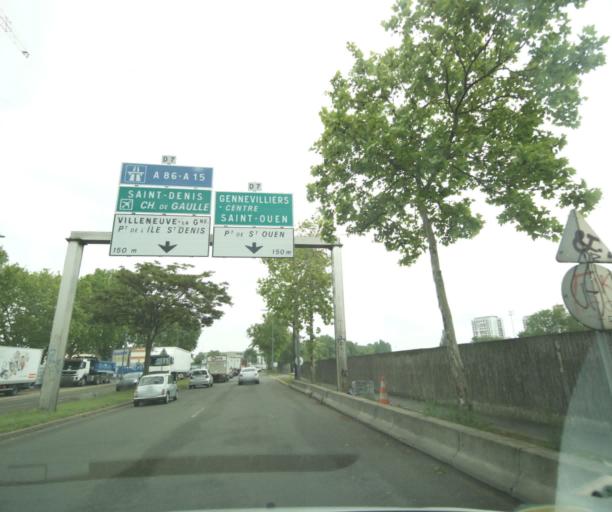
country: FR
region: Ile-de-France
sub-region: Departement des Hauts-de-Seine
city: Clichy
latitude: 48.9177
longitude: 2.3204
